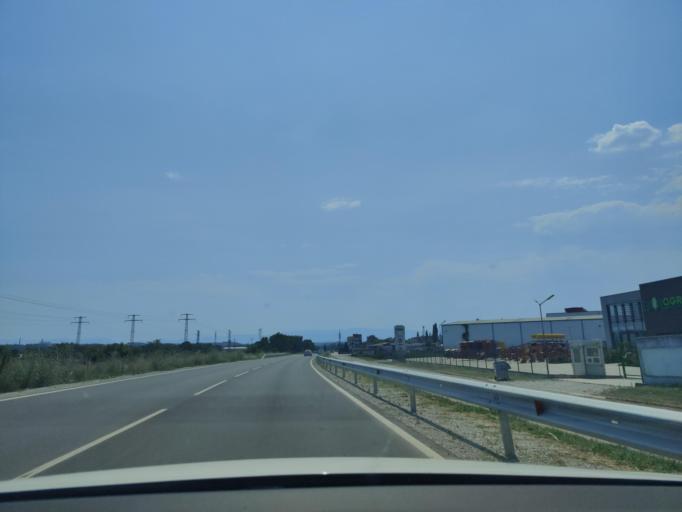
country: BG
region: Montana
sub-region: Obshtina Montana
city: Montana
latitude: 43.4254
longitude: 23.2400
